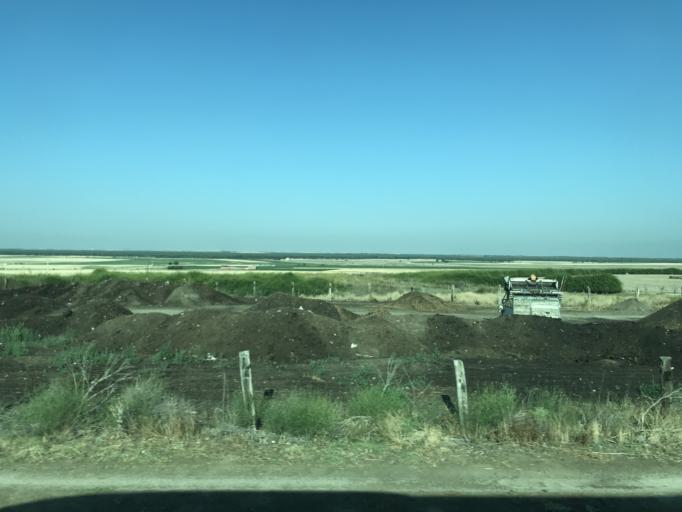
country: ES
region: Castille and Leon
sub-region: Provincia de Valladolid
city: Bocigas
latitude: 41.2381
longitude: -4.6726
